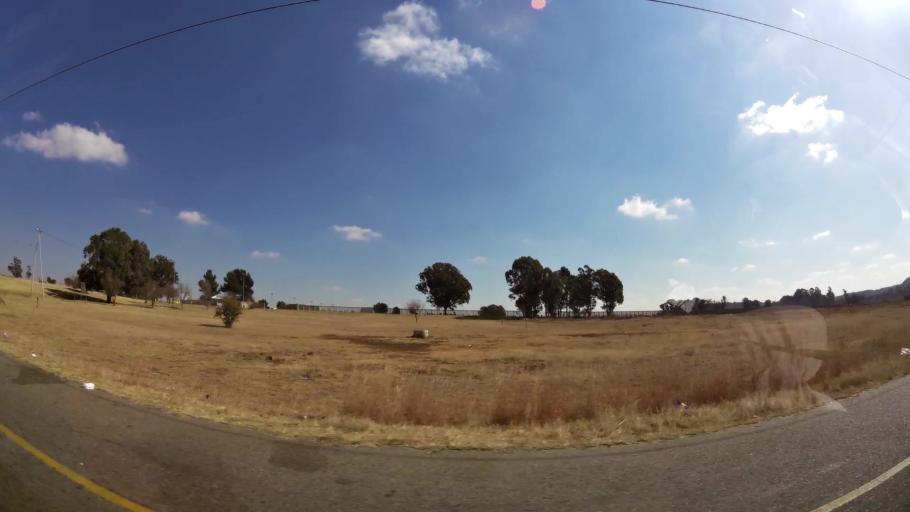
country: ZA
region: Gauteng
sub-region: West Rand District Municipality
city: Randfontein
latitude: -26.1555
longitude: 27.7624
